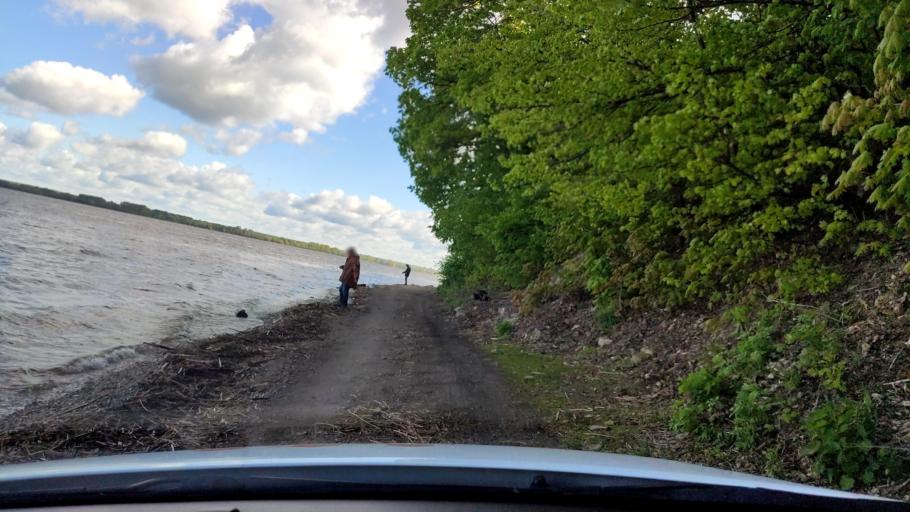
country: RU
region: Tatarstan
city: Sviyazhsk
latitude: 55.7802
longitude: 48.6964
